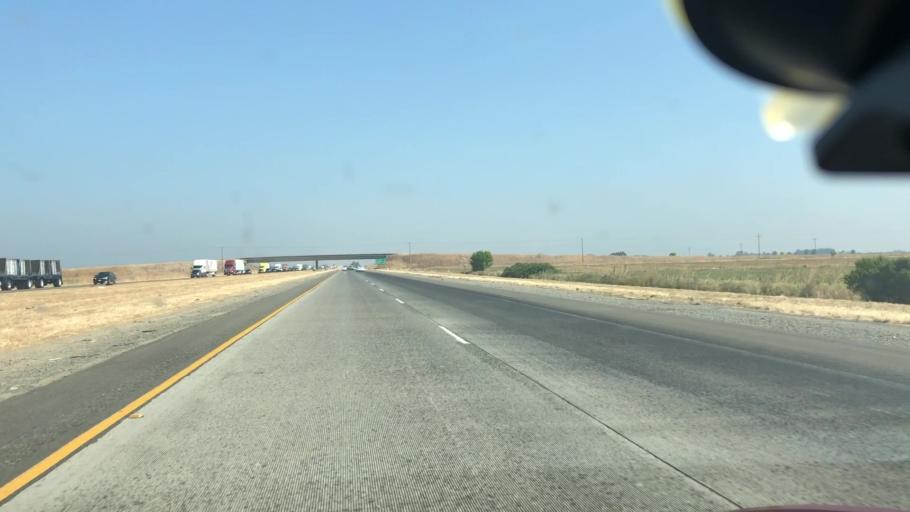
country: US
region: California
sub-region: Sacramento County
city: Walnut Grove
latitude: 38.2950
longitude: -121.4599
